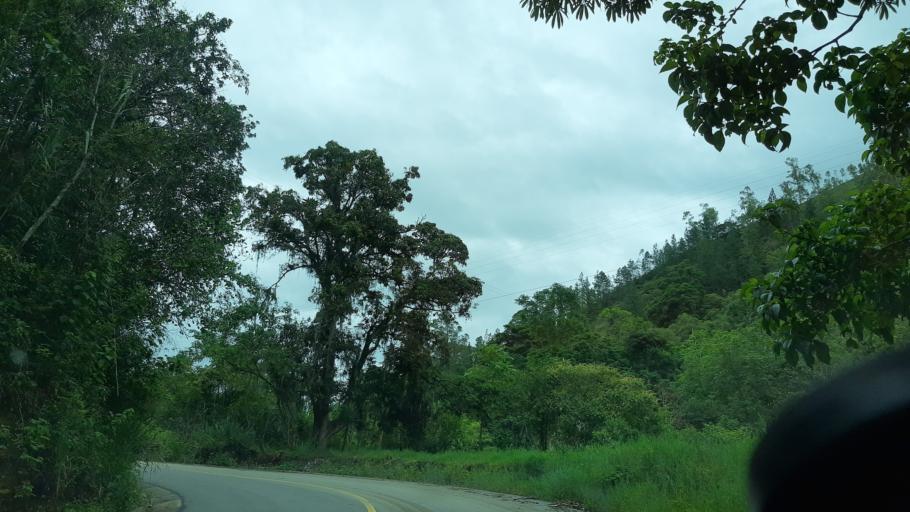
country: CO
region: Cundinamarca
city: Tenza
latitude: 5.0736
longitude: -73.4067
